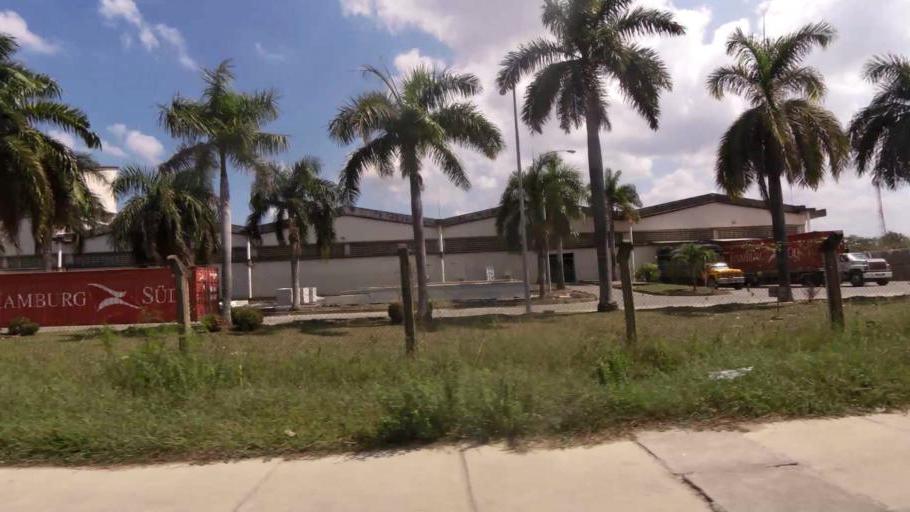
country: CO
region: Bolivar
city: Cartagena
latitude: 10.3515
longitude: -75.4957
